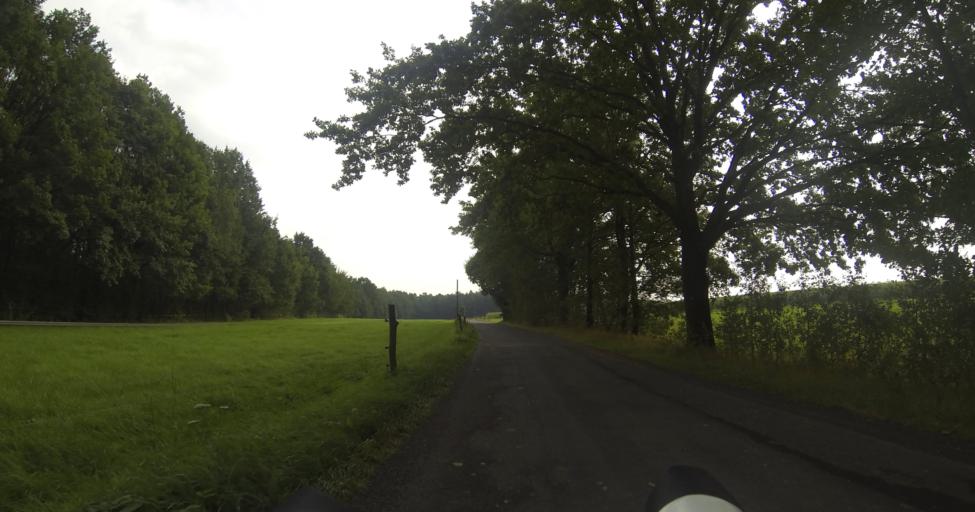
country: DE
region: Saxony
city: Weinbohla
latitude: 51.2055
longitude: 13.5940
